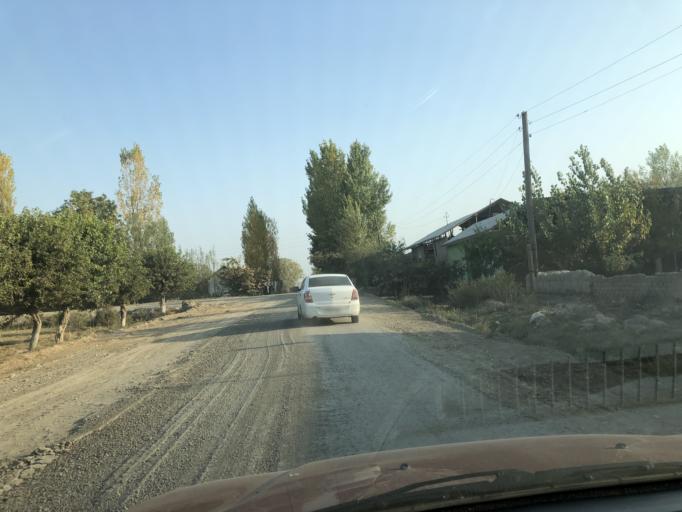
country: UZ
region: Namangan
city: Uychi
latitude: 41.0645
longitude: 71.9873
